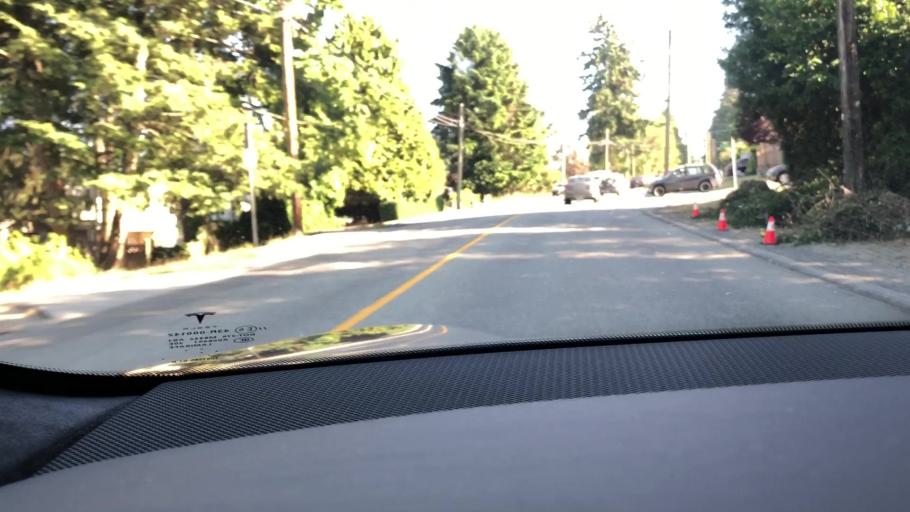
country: CA
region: British Columbia
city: Burnaby
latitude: 49.2555
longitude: -122.9822
